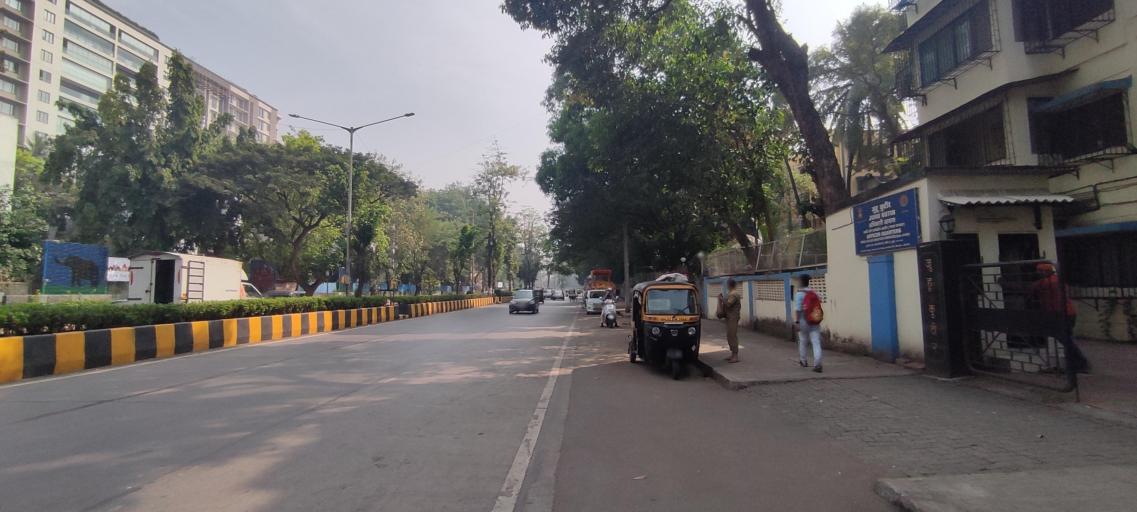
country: IN
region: Maharashtra
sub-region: Mumbai Suburban
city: Mumbai
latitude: 19.1194
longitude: 72.8281
